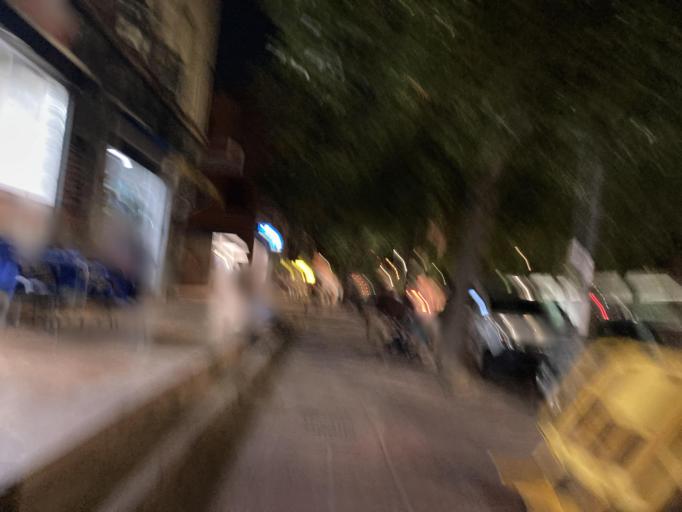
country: ES
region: Murcia
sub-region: Murcia
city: Murcia
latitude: 37.9979
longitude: -1.1314
